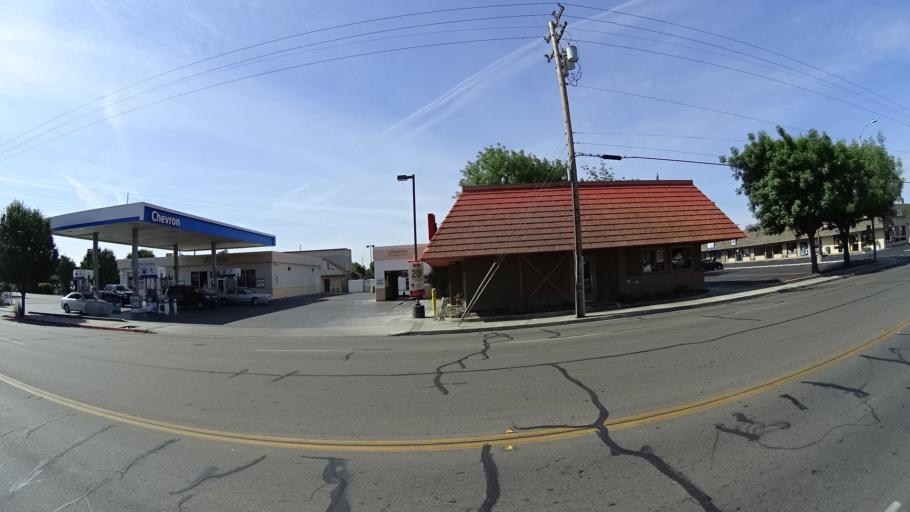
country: US
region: California
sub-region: Kings County
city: Hanford
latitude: 36.3427
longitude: -119.6556
